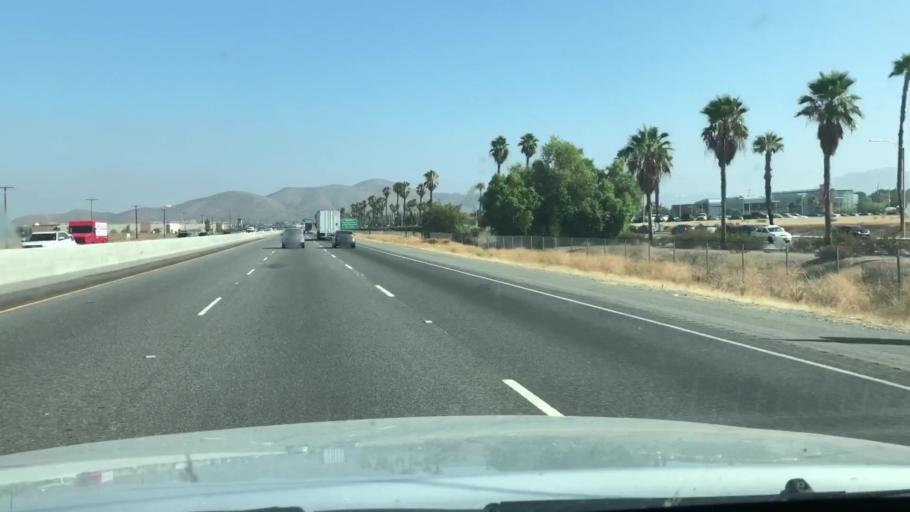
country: US
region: California
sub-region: Riverside County
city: Sun City
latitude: 33.6718
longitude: -117.1707
